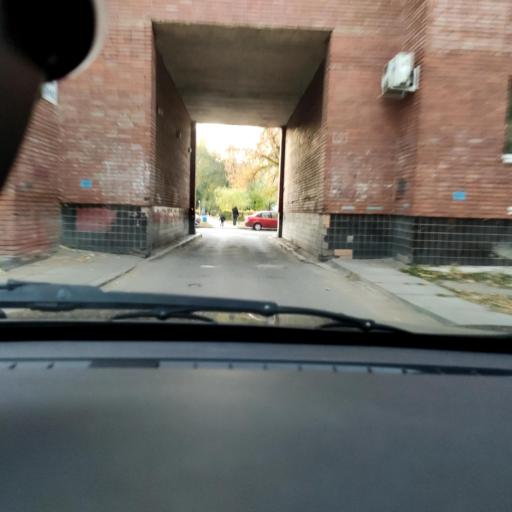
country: RU
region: Samara
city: Tol'yatti
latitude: 53.5362
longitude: 49.2727
